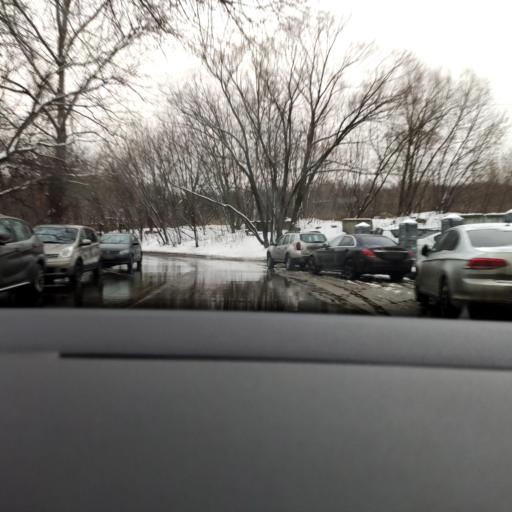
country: RU
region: Moscow
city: Metrogorodok
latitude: 55.8244
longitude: 37.7795
